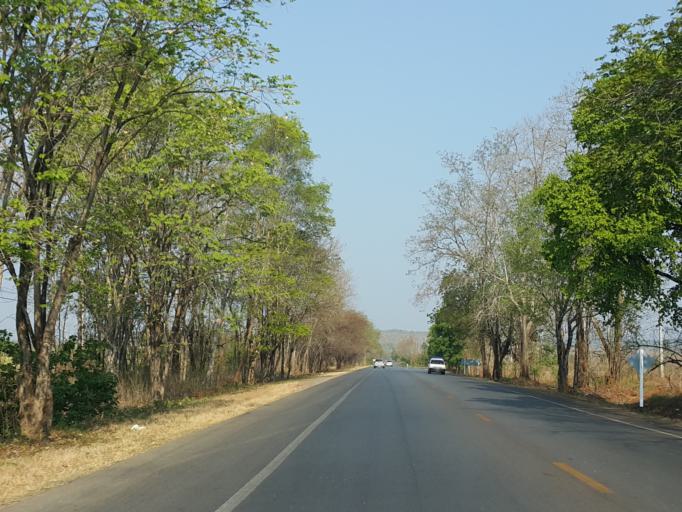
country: TH
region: Kanchanaburi
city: Sai Yok
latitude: 14.0965
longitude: 99.2492
